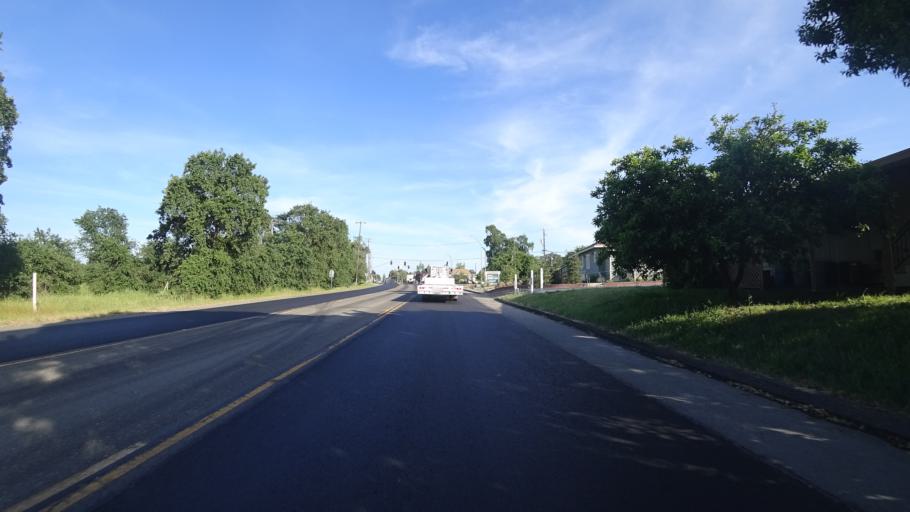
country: US
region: California
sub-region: Yuba County
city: Wheatland
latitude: 39.0116
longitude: -121.4280
